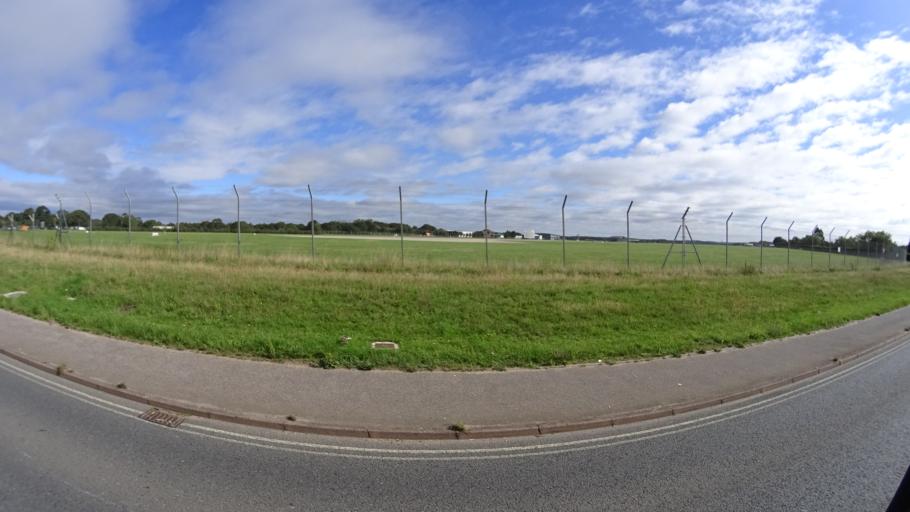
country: GB
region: England
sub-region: Dorset
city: Ferndown
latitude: 50.7762
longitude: -1.8581
